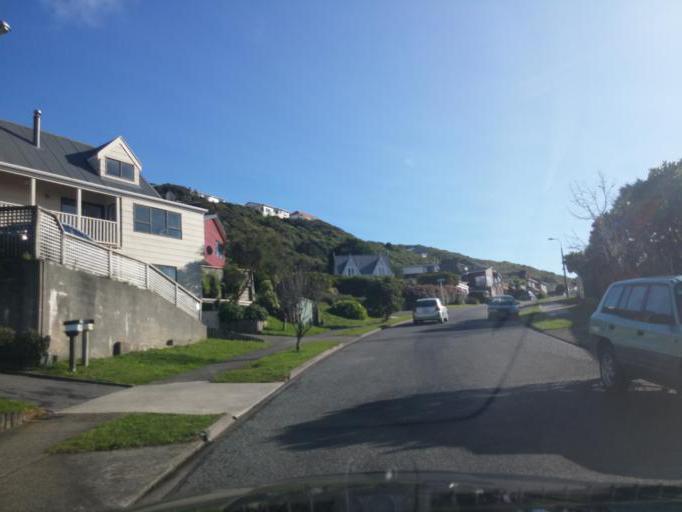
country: NZ
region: Wellington
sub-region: Wellington City
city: Wellington
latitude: -41.2342
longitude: 174.7935
